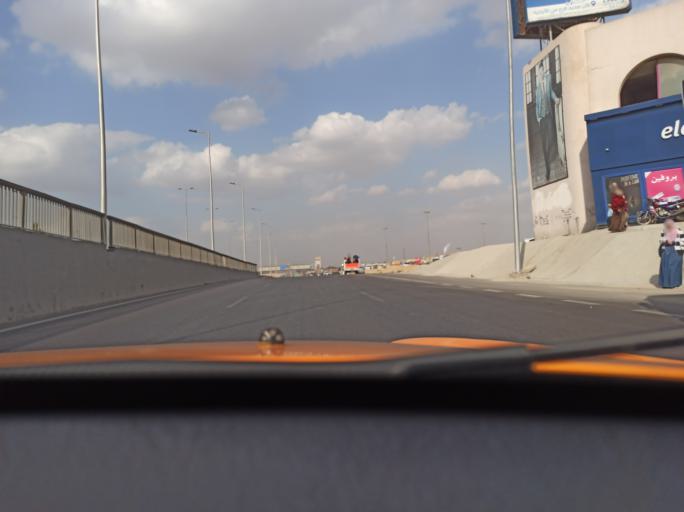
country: EG
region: Eastern Province
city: Bilbays
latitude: 30.2421
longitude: 31.7225
